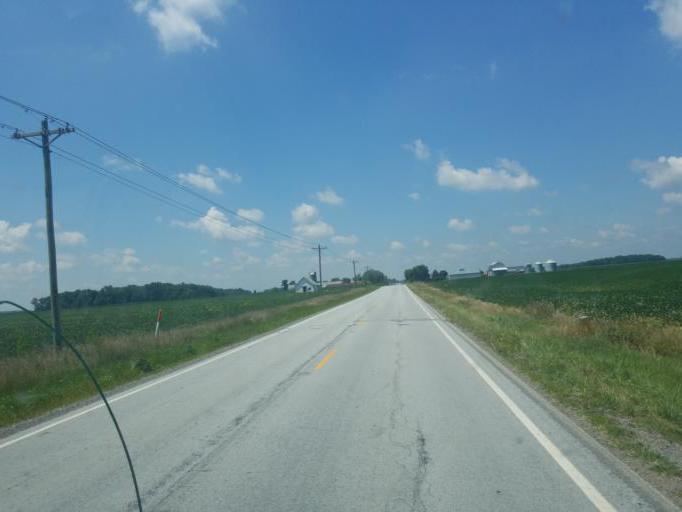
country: US
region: Ohio
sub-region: Allen County
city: Spencerville
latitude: 40.7141
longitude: -84.4029
